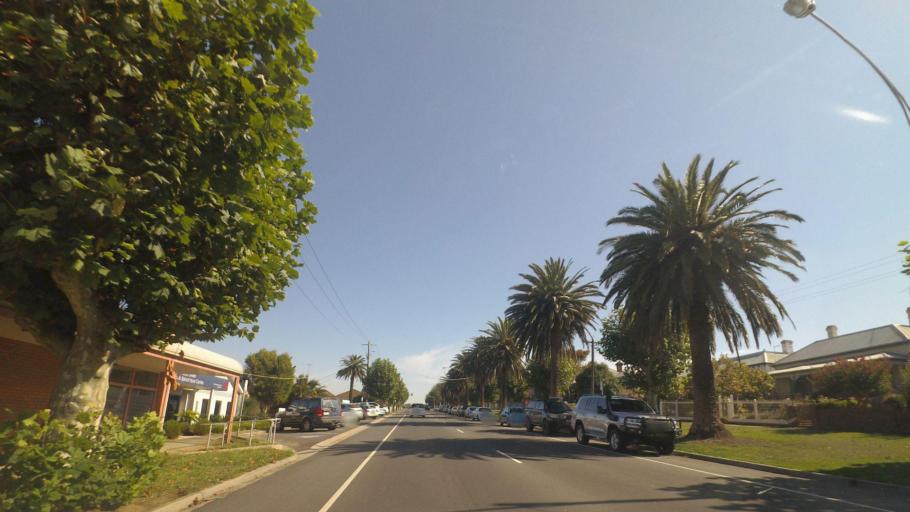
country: AU
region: Victoria
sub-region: Baw Baw
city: Warragul
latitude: -38.1594
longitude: 145.9321
